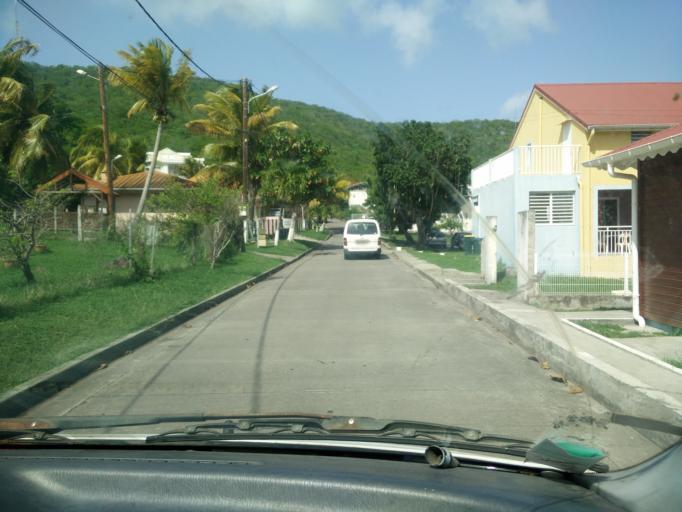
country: GP
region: Guadeloupe
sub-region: Guadeloupe
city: Terre-de-Bas
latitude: 15.8508
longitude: -61.6432
